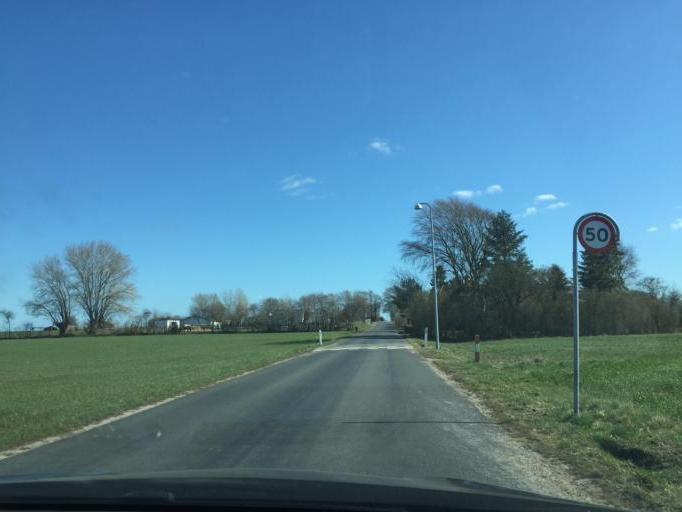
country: DK
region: South Denmark
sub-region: Faaborg-Midtfyn Kommune
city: Arslev
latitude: 55.3405
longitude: 10.5181
